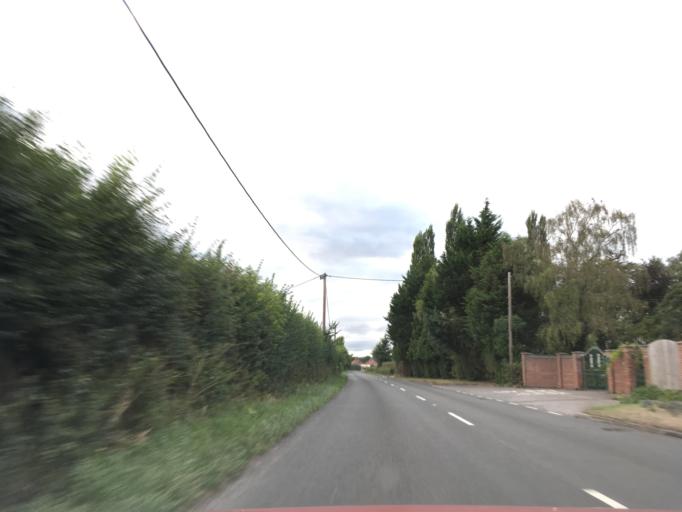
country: GB
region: England
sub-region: Wiltshire
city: Devizes
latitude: 51.3594
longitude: -2.0147
